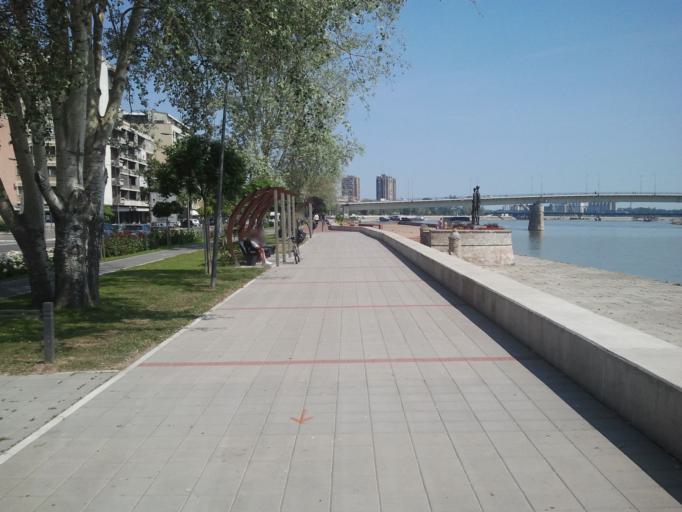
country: RS
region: Autonomna Pokrajina Vojvodina
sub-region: Juznobacki Okrug
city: Novi Sad
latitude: 45.2515
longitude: 19.8559
